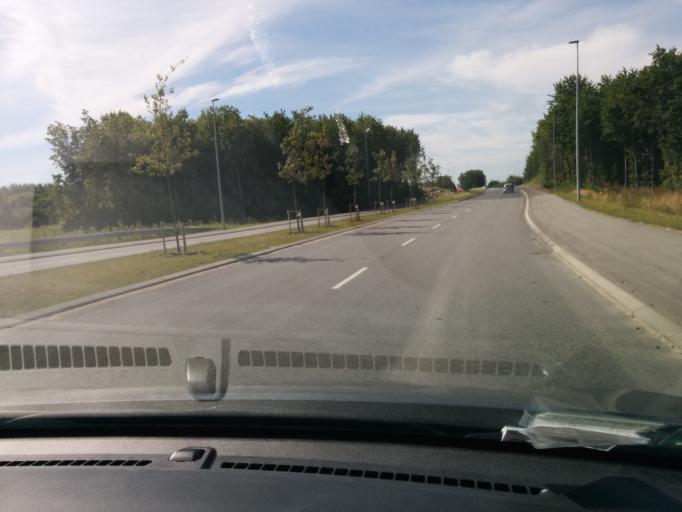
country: DK
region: Central Jutland
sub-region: Arhus Kommune
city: Arhus
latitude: 56.1855
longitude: 10.1704
